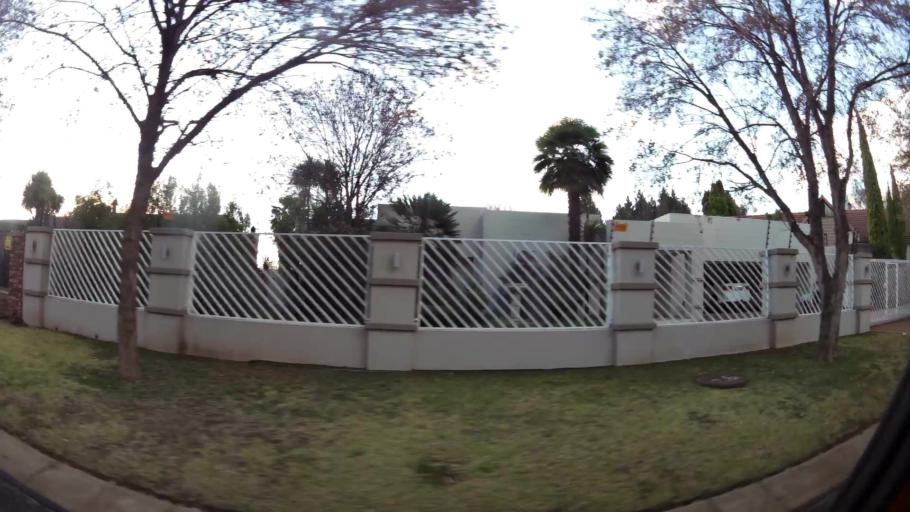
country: ZA
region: North-West
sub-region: Dr Kenneth Kaunda District Municipality
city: Potchefstroom
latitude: -26.6793
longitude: 27.1082
